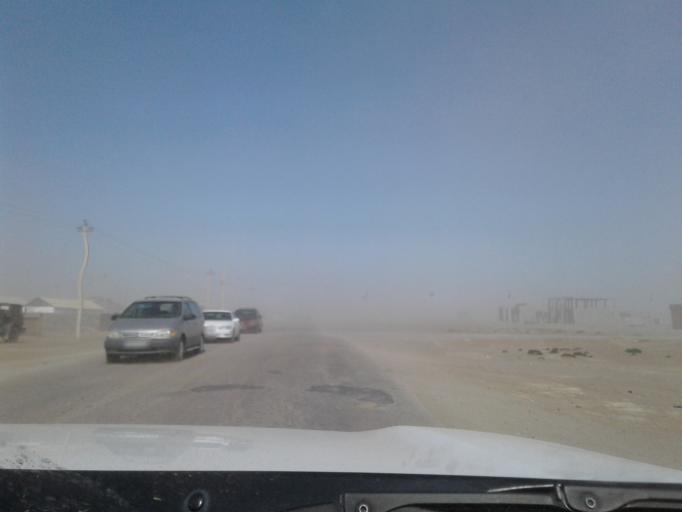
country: TM
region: Balkan
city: Gumdag
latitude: 39.1924
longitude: 54.5873
